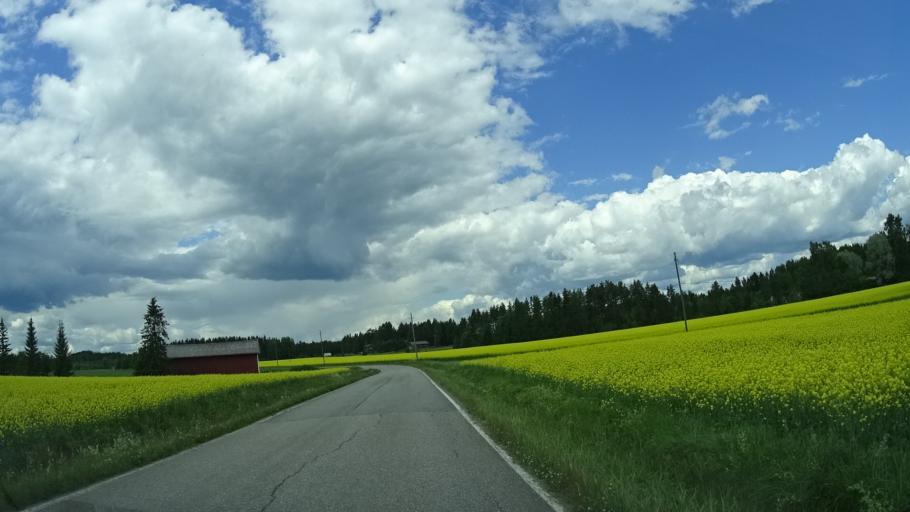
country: FI
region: Uusimaa
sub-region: Helsinki
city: Espoo
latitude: 60.4048
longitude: 24.6112
